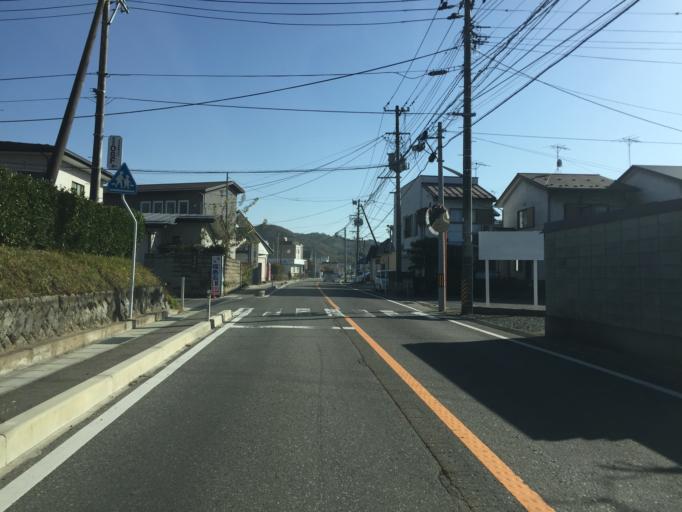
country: JP
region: Fukushima
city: Fukushima-shi
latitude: 37.7380
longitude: 140.4718
